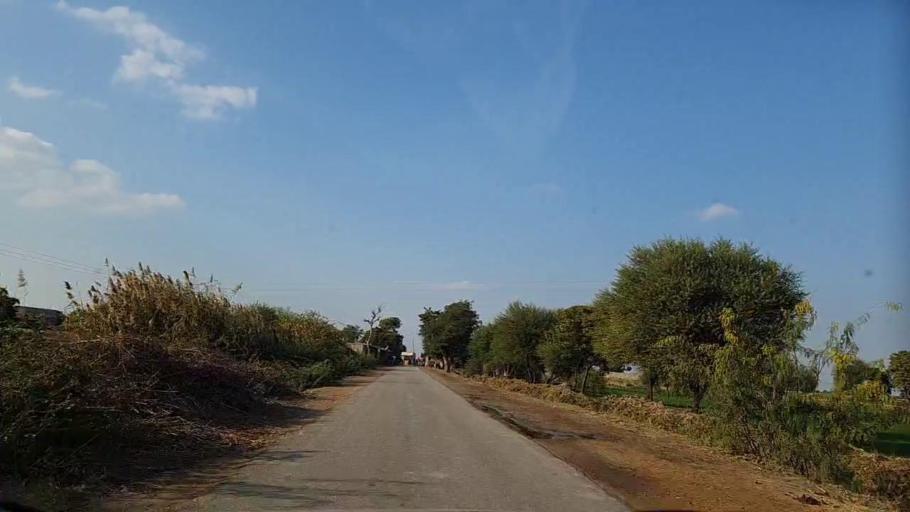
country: PK
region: Sindh
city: Tando Mittha Khan
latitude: 25.7323
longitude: 69.2118
